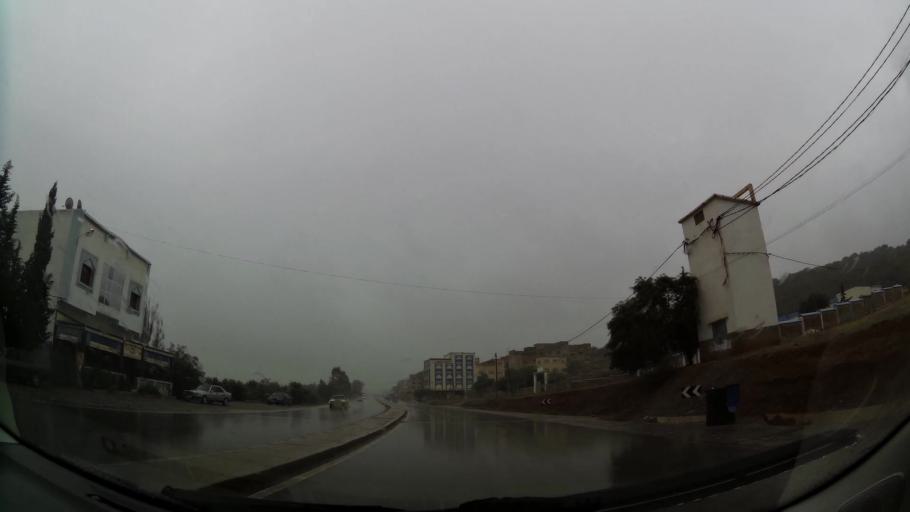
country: MA
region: Taza-Al Hoceima-Taounate
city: Imzourene
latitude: 35.1248
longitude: -3.8456
